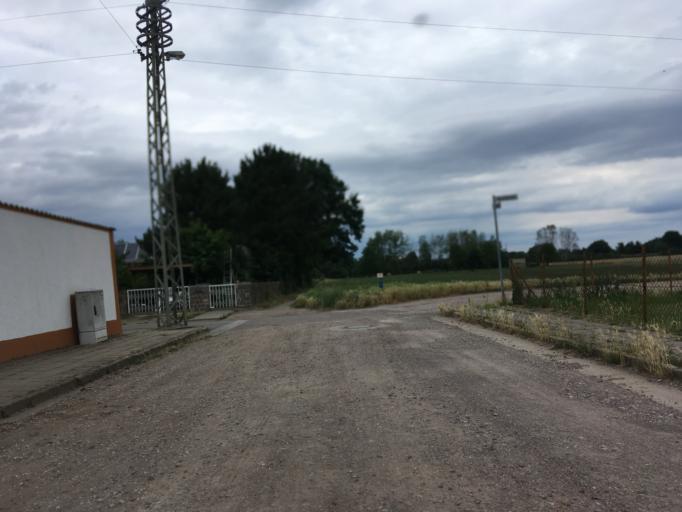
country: DE
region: Saxony-Anhalt
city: Quellendorf
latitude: 51.8129
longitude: 12.1541
